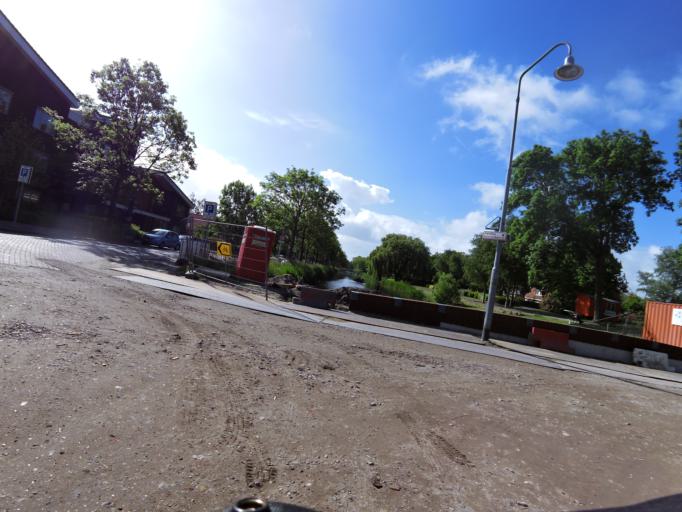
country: NL
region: Zeeland
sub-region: Schouwen-Duiveland
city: Scharendijke
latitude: 51.6527
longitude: 3.9240
